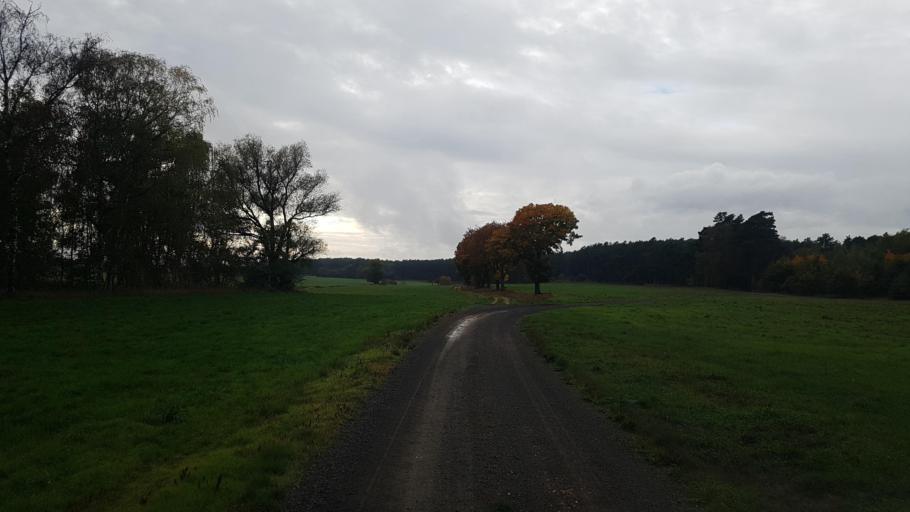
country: DE
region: Brandenburg
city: Schlieben
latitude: 51.7364
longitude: 13.3529
